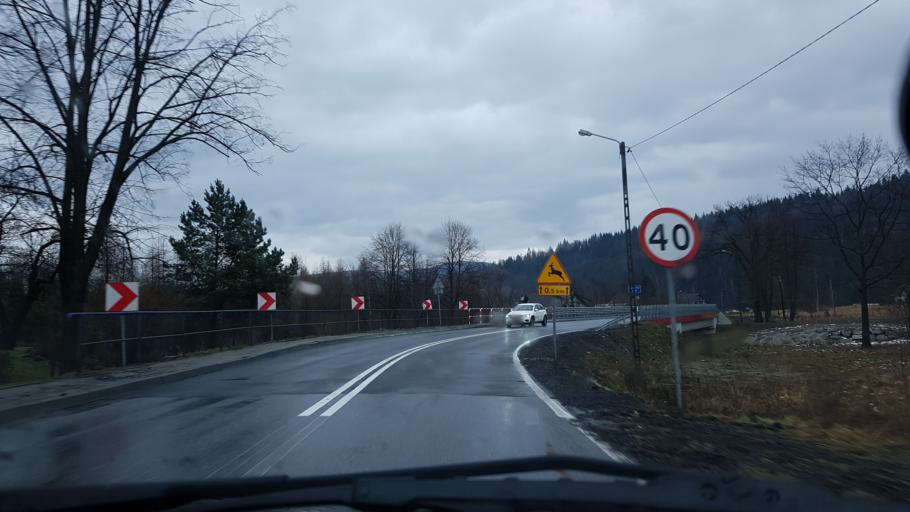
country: PL
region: Lesser Poland Voivodeship
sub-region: Powiat suski
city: Kukow
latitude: 49.7307
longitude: 19.4893
